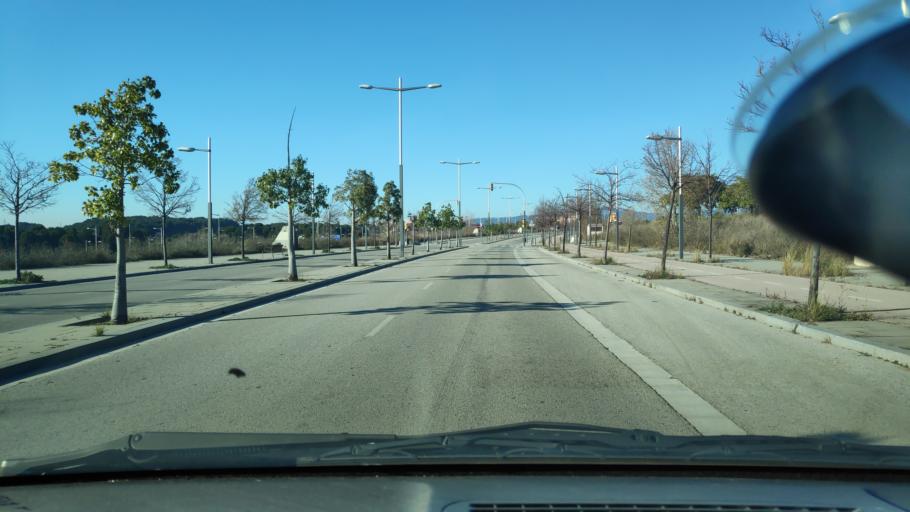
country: ES
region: Catalonia
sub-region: Provincia de Barcelona
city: Sant Quirze del Valles
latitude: 41.5422
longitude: 2.0835
